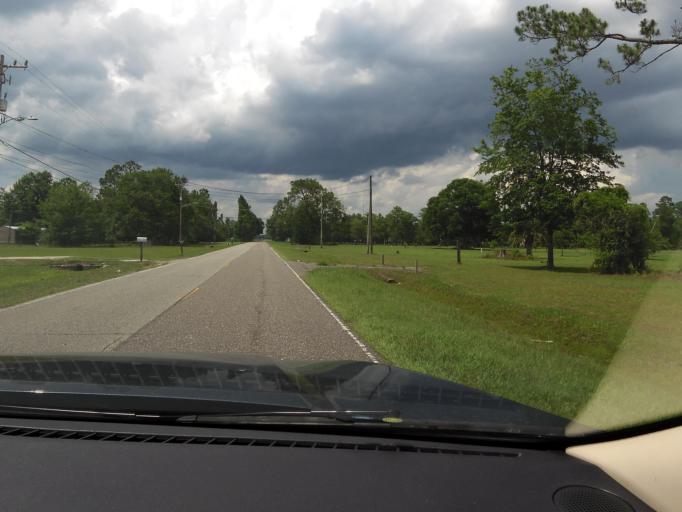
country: US
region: Florida
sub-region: Duval County
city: Baldwin
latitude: 30.3162
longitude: -81.8694
